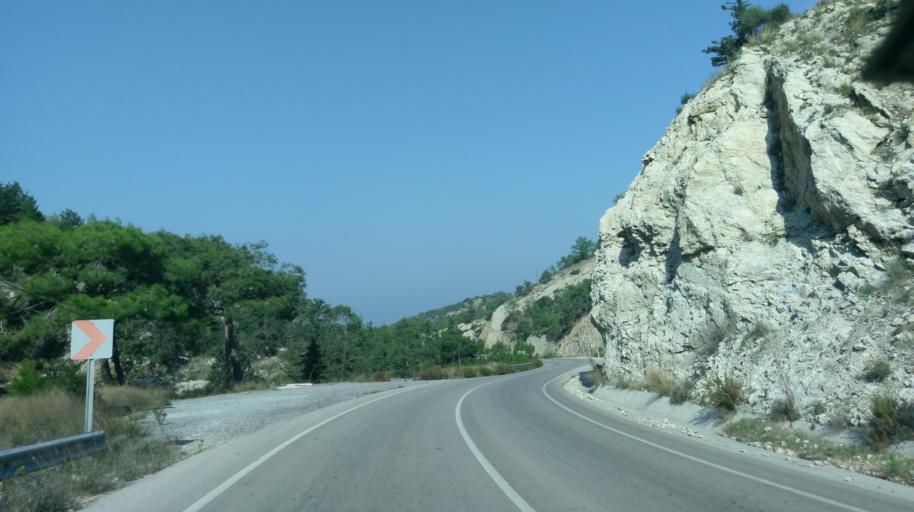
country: CY
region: Ammochostos
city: Lefkonoiko
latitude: 35.3499
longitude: 33.7148
